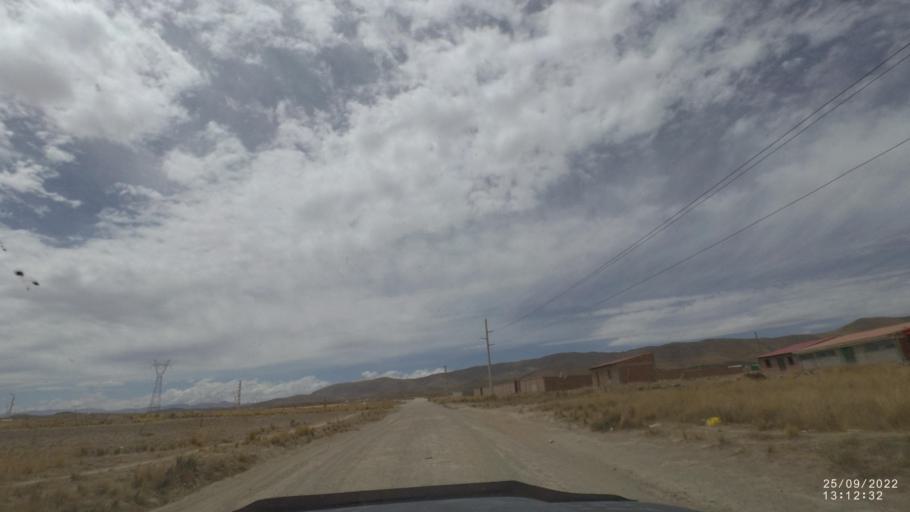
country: BO
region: Oruro
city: Oruro
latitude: -17.9564
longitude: -67.0407
